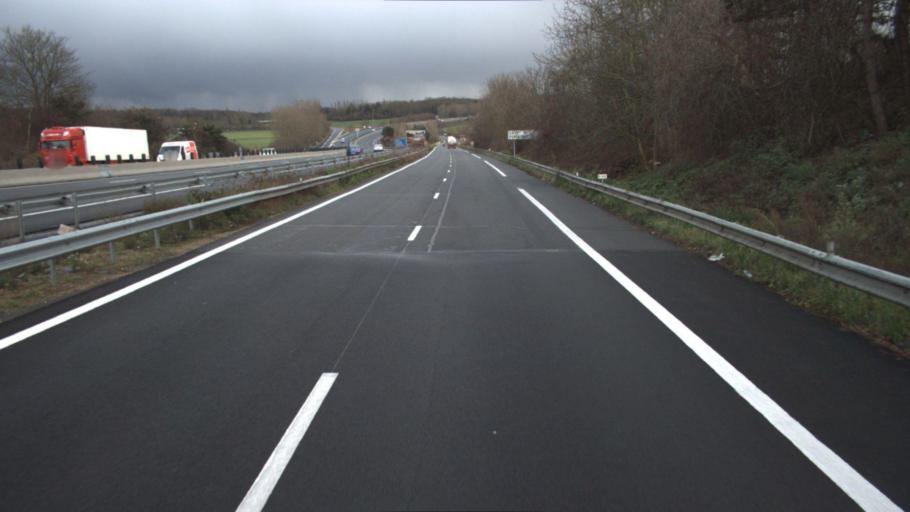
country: FR
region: Ile-de-France
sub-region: Departement de l'Essonne
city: Soisy-sur-Ecole
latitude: 48.4812
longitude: 2.5140
